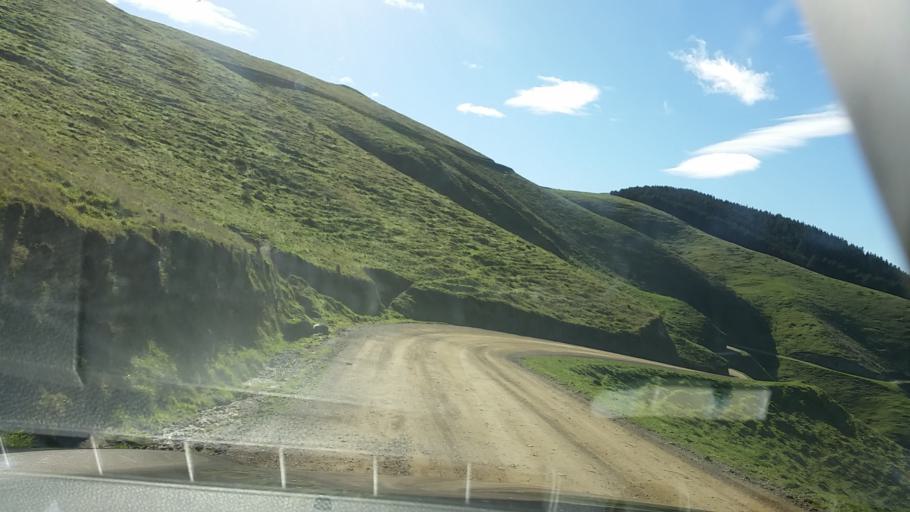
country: NZ
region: Marlborough
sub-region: Marlborough District
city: Picton
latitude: -40.9883
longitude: 173.8074
